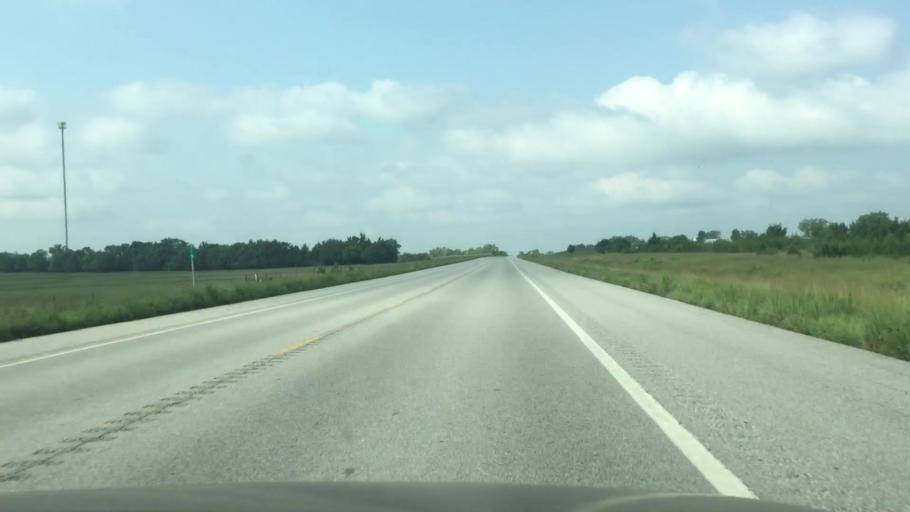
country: US
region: Kansas
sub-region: Miami County
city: Osawatomie
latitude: 38.4109
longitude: -95.0498
